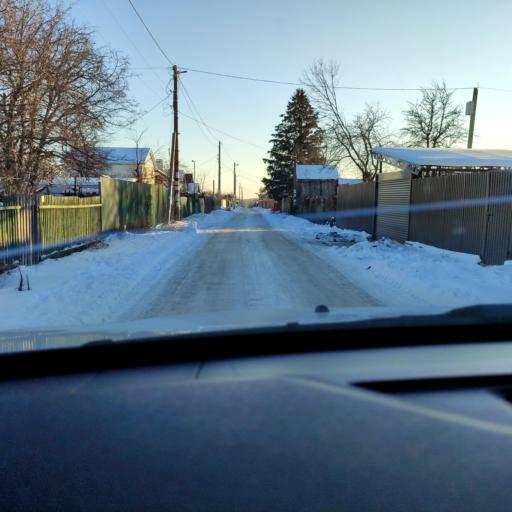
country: RU
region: Samara
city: Petra-Dubrava
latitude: 53.2853
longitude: 50.2915
